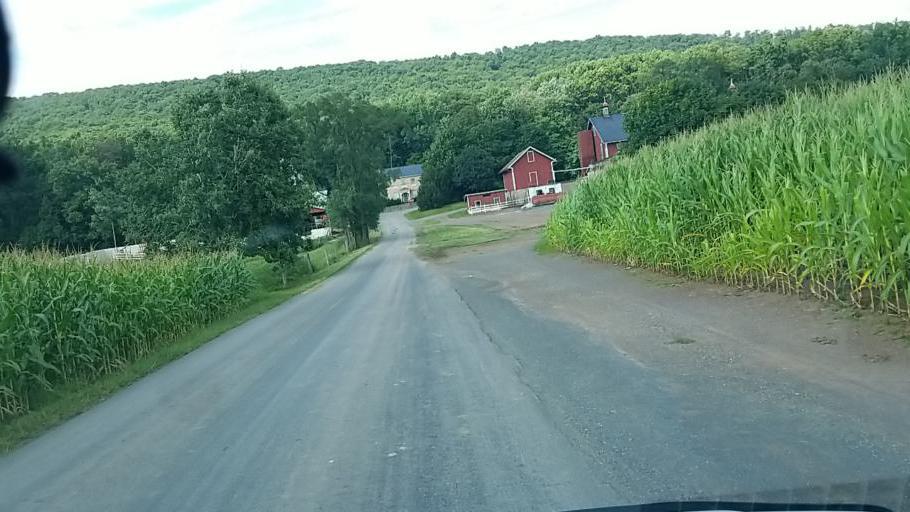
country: US
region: Pennsylvania
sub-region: Dauphin County
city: Elizabethville
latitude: 40.6090
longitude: -76.8535
